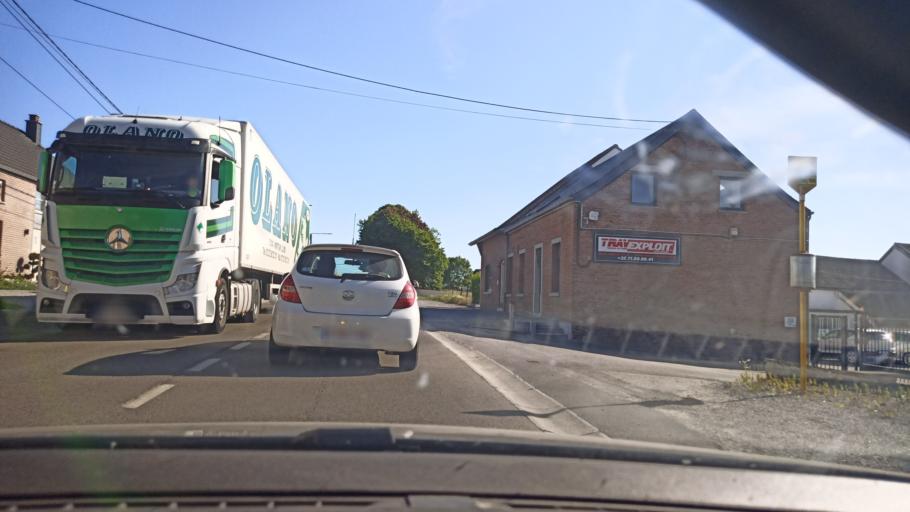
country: BE
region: Wallonia
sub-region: Province du Hainaut
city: Lobbes
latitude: 50.3386
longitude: 4.2674
